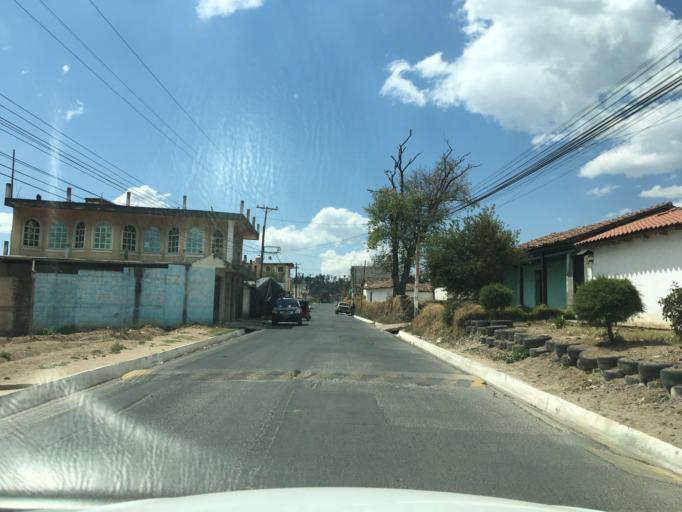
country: GT
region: Totonicapan
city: San Cristobal Totonicapan
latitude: 14.9086
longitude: -91.4523
